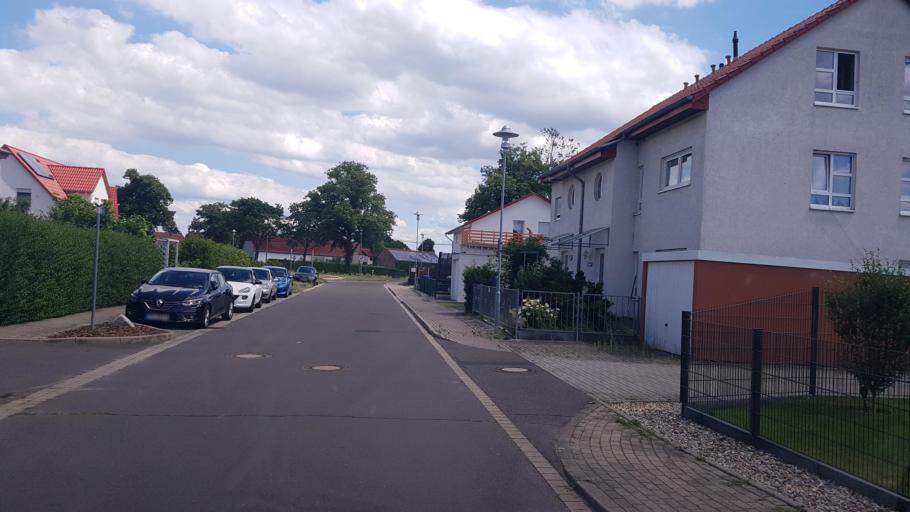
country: DE
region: Brandenburg
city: Trebbin
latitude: 52.1936
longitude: 13.2396
